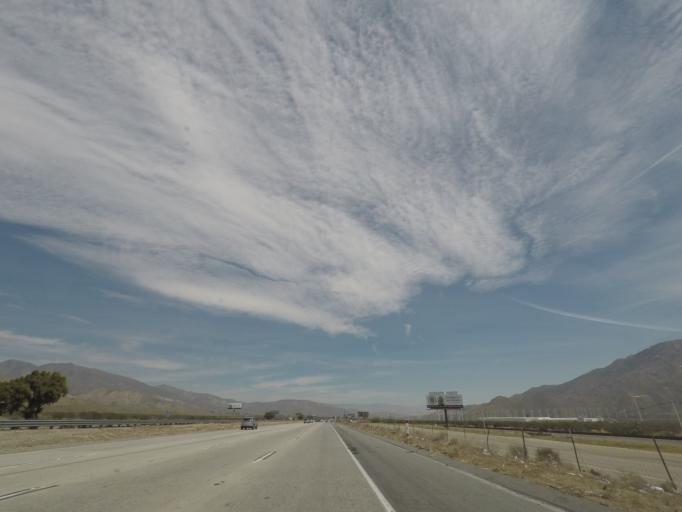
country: US
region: California
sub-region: Riverside County
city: Cabazon
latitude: 33.9205
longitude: -116.7646
